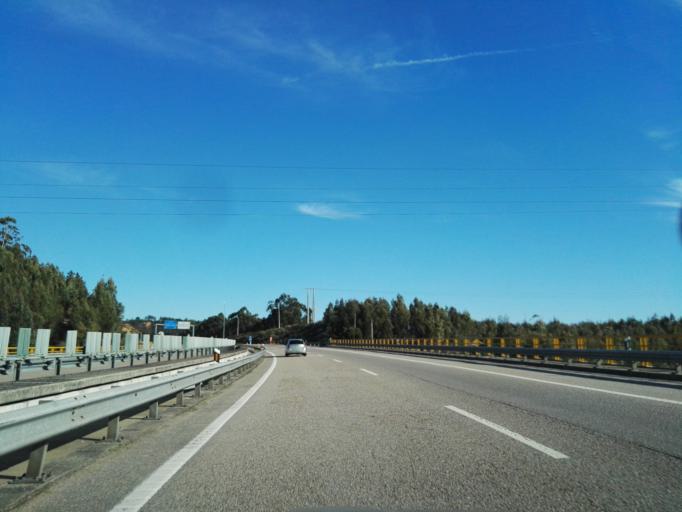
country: PT
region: Santarem
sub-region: Abrantes
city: Abrantes
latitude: 39.4794
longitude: -8.2313
